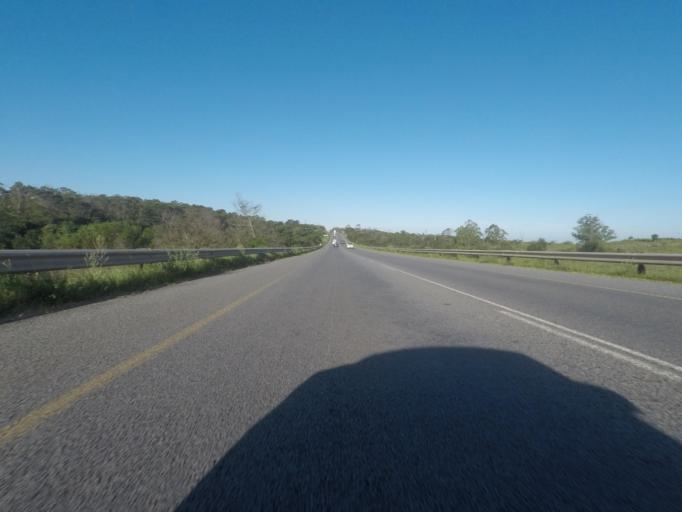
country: ZA
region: Eastern Cape
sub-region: Buffalo City Metropolitan Municipality
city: East London
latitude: -33.0513
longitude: 27.8125
